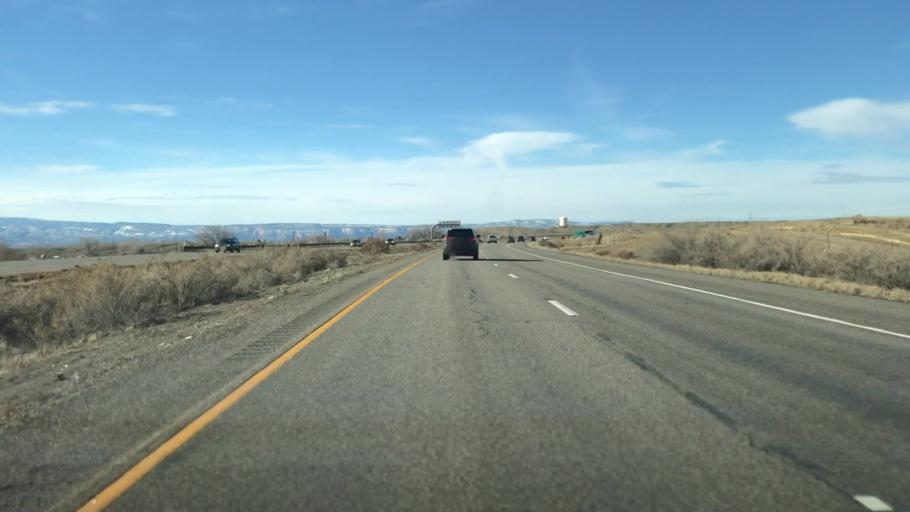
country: US
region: Colorado
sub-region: Mesa County
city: Clifton
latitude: 39.1082
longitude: -108.4284
